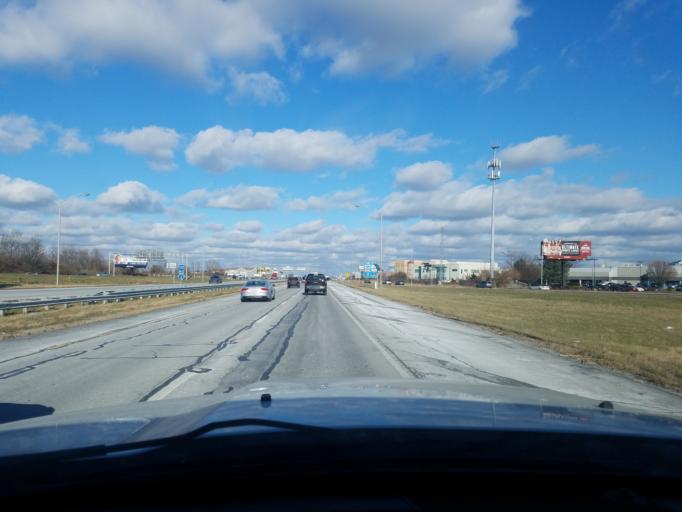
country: US
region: Indiana
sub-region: Marion County
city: Lawrence
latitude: 39.8966
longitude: -86.0526
